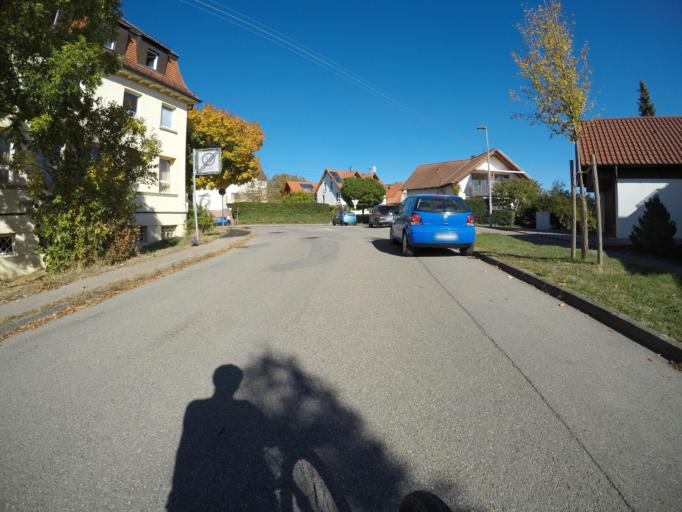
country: DE
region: Baden-Wuerttemberg
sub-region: Regierungsbezirk Stuttgart
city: Herrenberg
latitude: 48.5802
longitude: 8.8401
